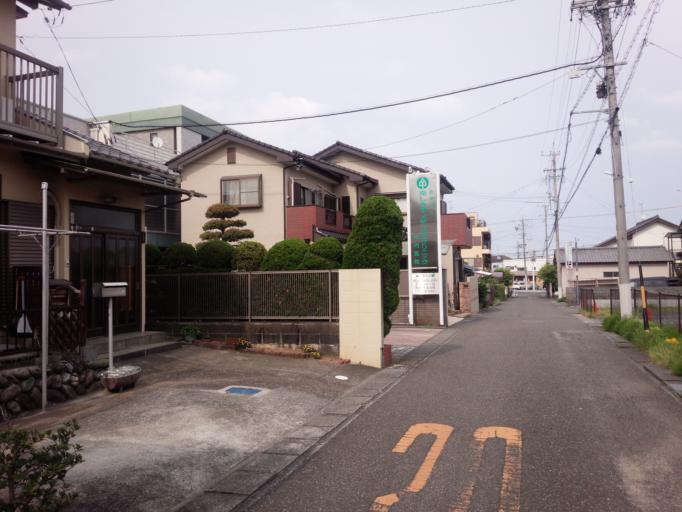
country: JP
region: Shizuoka
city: Shizuoka-shi
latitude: 34.9963
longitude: 138.4810
